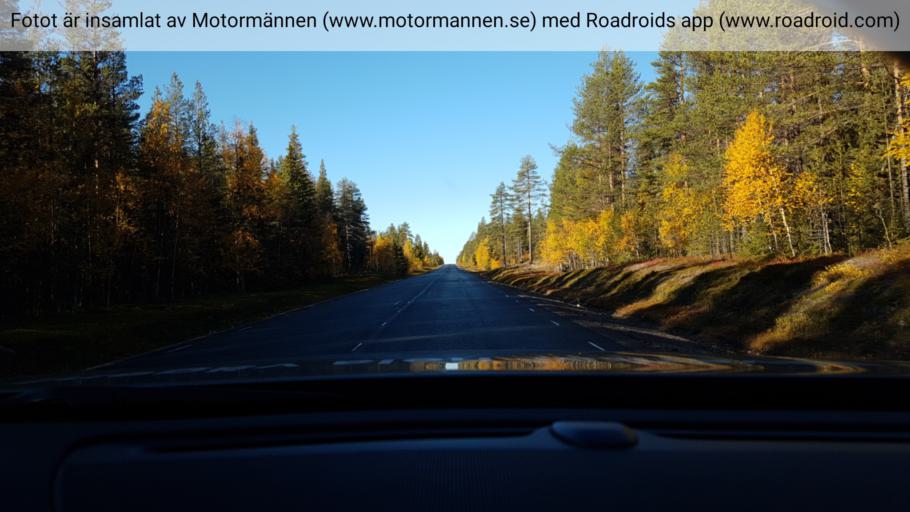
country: SE
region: Vaesterbotten
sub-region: Norsjo Kommun
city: Norsjoe
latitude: 65.4153
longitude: 19.8592
